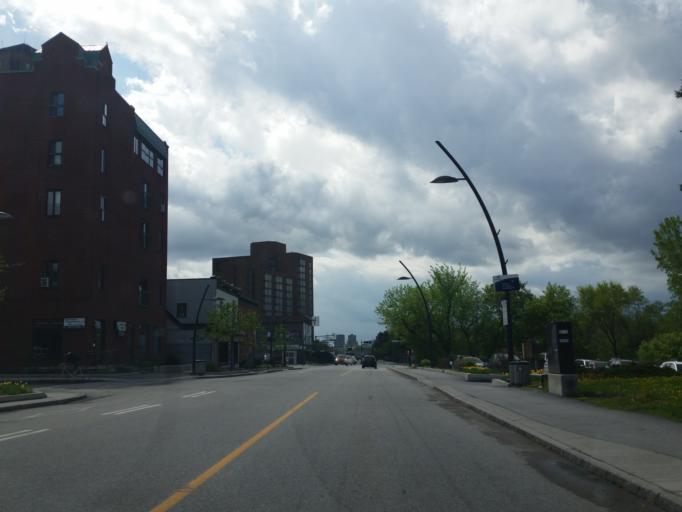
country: CA
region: Ontario
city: Ottawa
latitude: 45.4274
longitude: -75.7247
